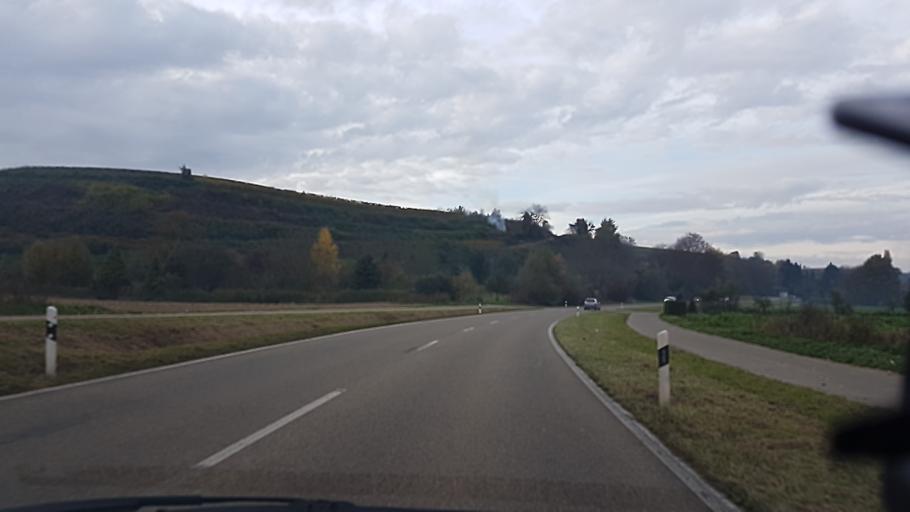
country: DE
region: Baden-Wuerttemberg
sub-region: Freiburg Region
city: Bahlingen
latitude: 48.1142
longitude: 7.7428
